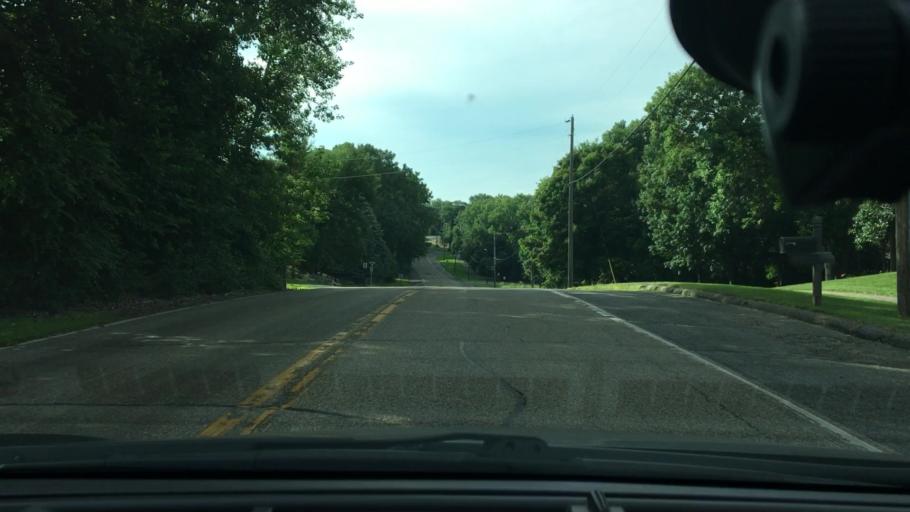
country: US
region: Minnesota
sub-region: Hennepin County
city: Plymouth
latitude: 45.0108
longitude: -93.4350
